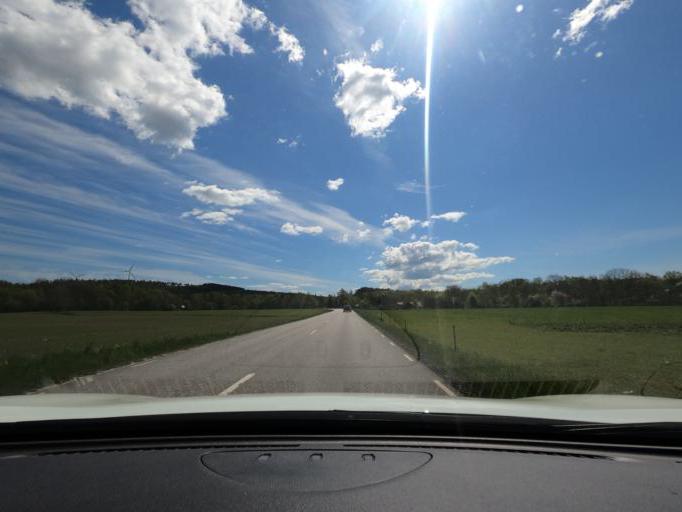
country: SE
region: Halland
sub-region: Kungsbacka Kommun
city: Fjaeras kyrkby
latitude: 57.4197
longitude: 12.2042
